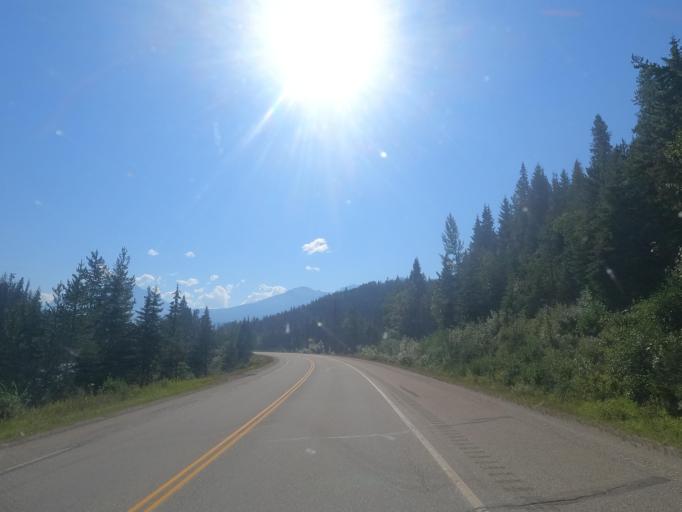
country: CA
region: Alberta
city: Jasper Park Lodge
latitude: 52.8601
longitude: -118.6395
